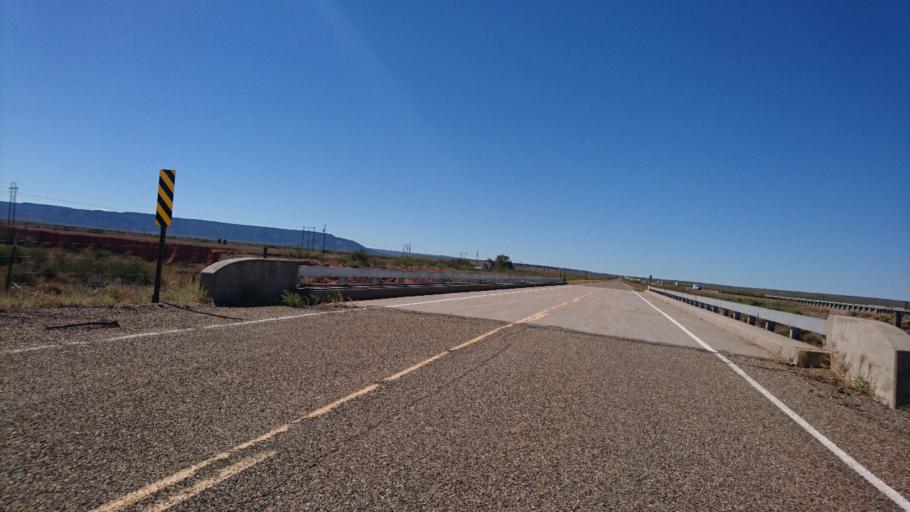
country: US
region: New Mexico
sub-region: Quay County
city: Tucumcari
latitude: 35.0915
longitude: -104.0762
